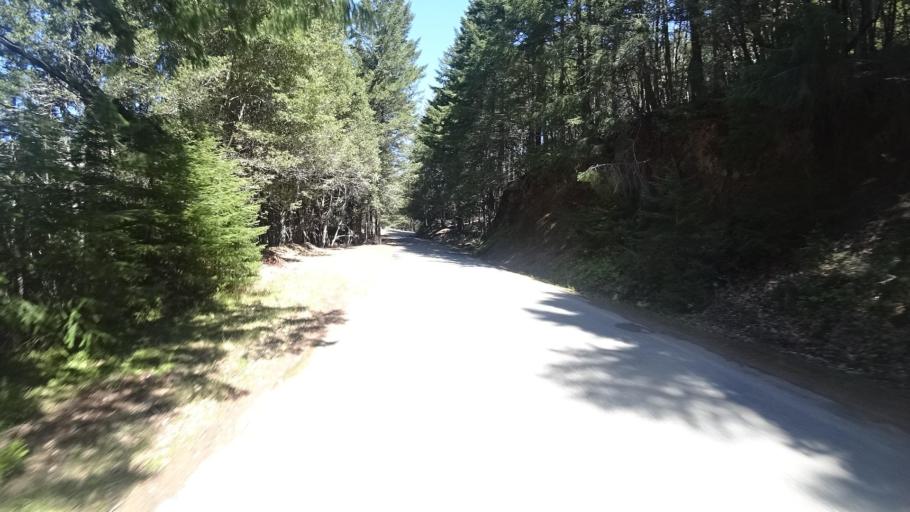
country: US
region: California
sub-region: Humboldt County
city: Rio Dell
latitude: 40.2848
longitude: -124.0573
